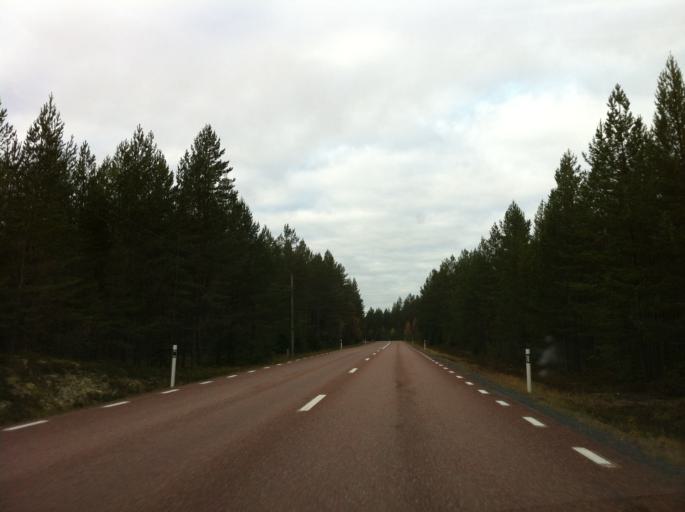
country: SE
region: Dalarna
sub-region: Alvdalens Kommun
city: AElvdalen
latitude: 61.1092
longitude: 14.2734
